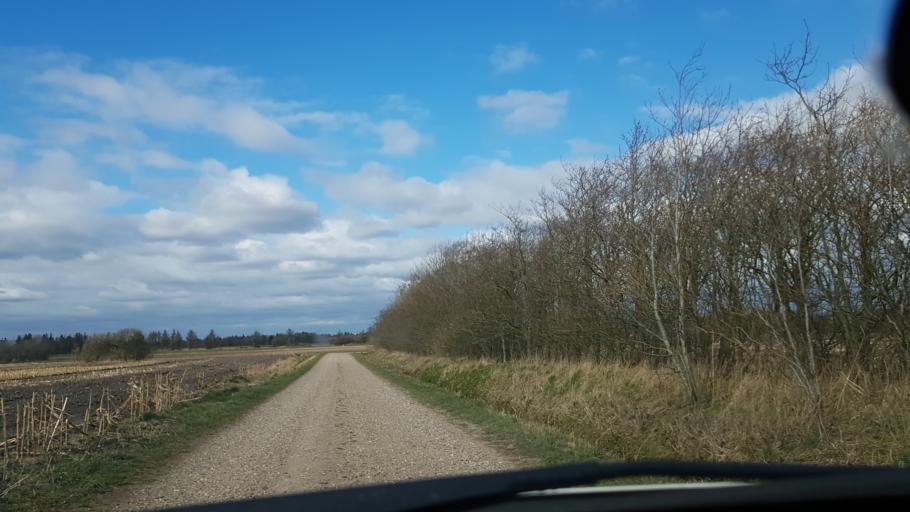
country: DK
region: South Denmark
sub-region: Esbjerg Kommune
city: Ribe
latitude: 55.2856
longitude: 8.8099
